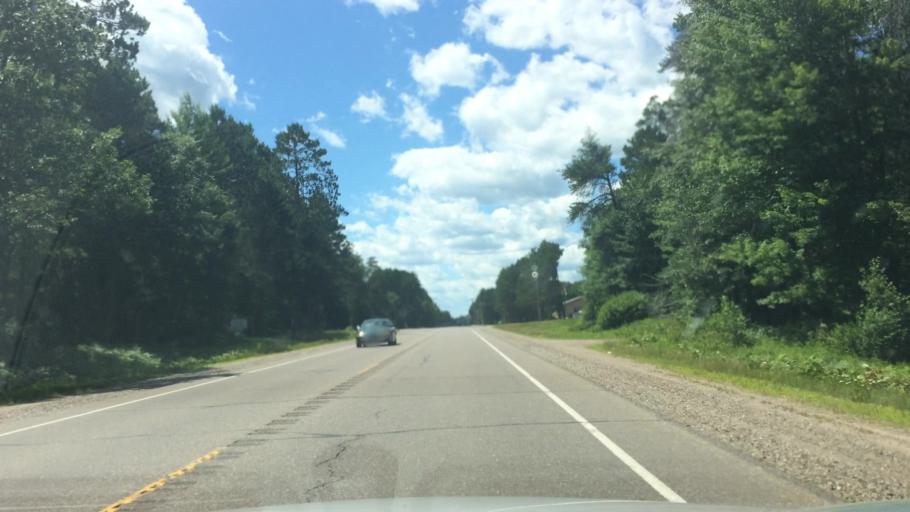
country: US
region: Wisconsin
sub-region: Vilas County
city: Lac du Flambeau
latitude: 45.8834
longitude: -89.7441
